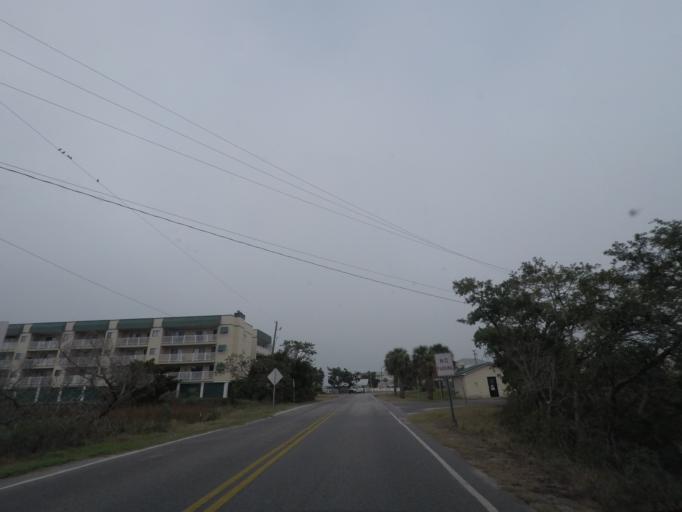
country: US
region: South Carolina
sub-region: Charleston County
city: Seabrook Island
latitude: 32.4932
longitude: -80.3415
